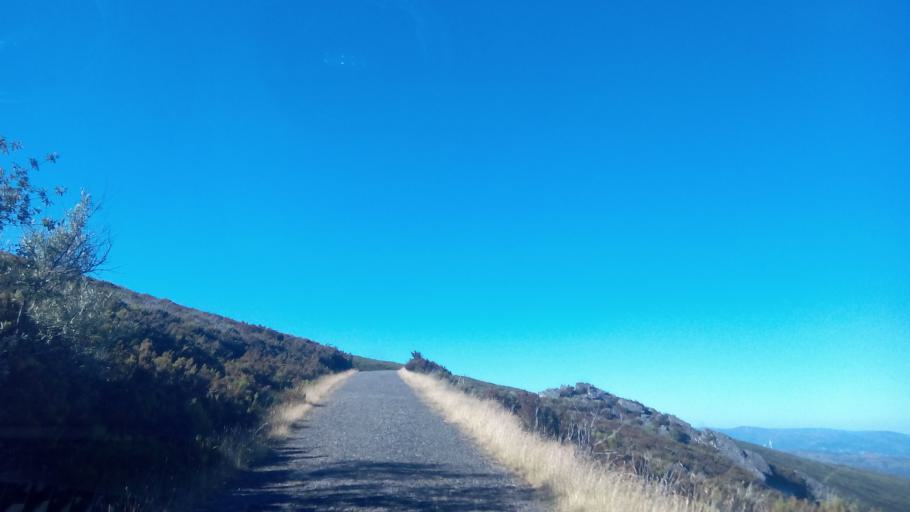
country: PT
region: Vila Real
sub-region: Mesao Frio
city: Mesao Frio
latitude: 41.2596
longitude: -7.8973
